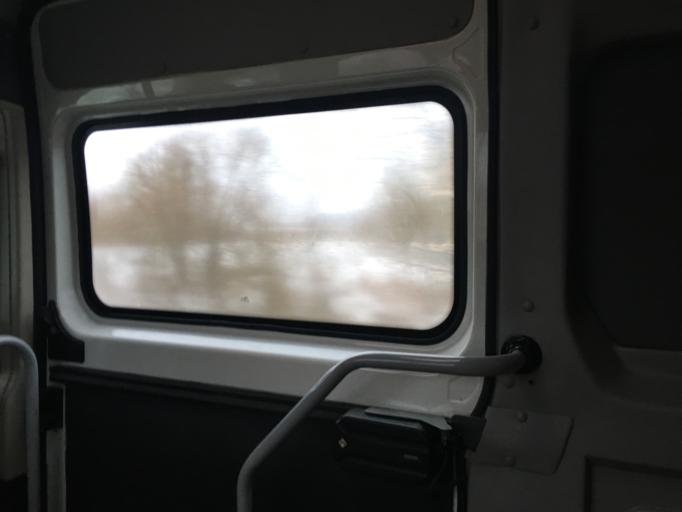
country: RU
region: Tula
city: Krapivna
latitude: 54.1139
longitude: 37.1513
